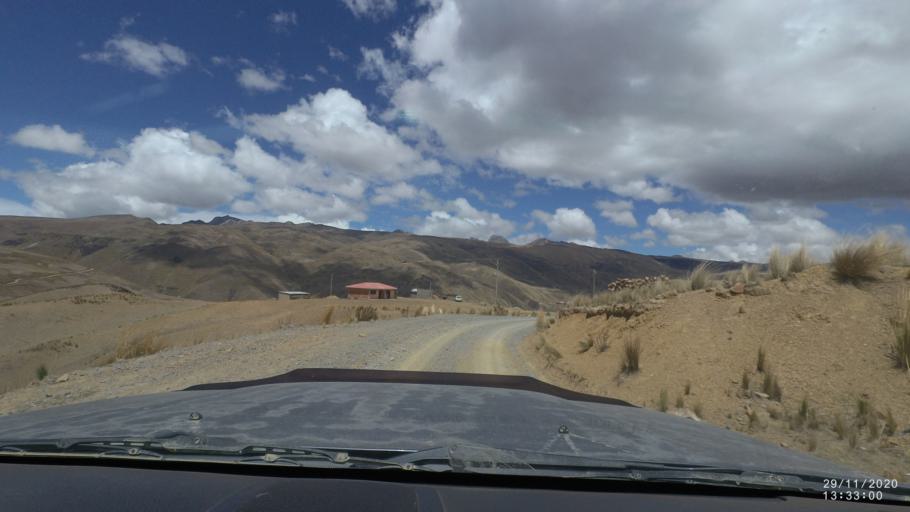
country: BO
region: Cochabamba
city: Cochabamba
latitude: -17.1050
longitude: -66.3389
